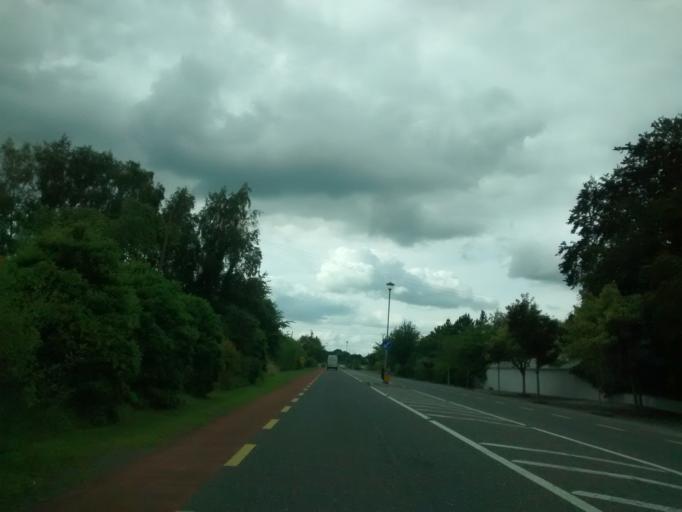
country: IE
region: Leinster
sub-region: Uibh Fhaili
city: Clara
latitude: 53.3749
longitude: -7.6585
